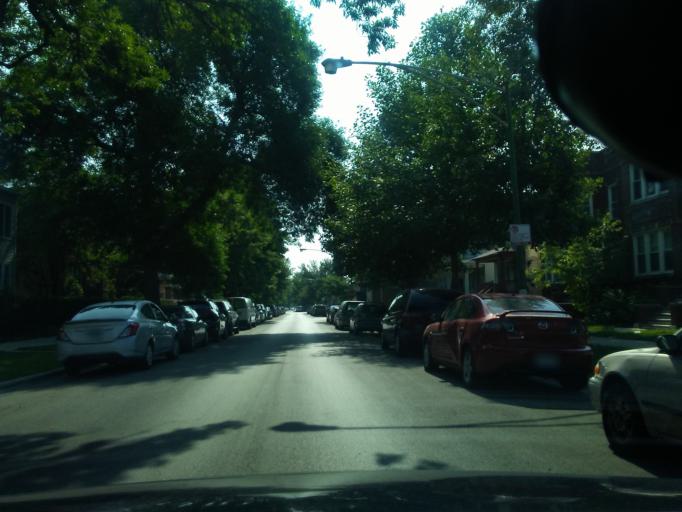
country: US
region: Illinois
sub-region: Cook County
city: Elmwood Park
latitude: 41.9277
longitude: -87.7633
